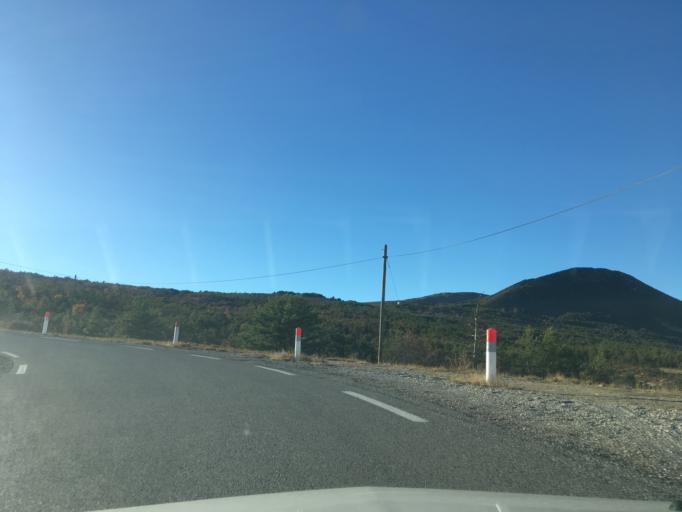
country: FR
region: Provence-Alpes-Cote d'Azur
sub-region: Departement des Alpes-de-Haute-Provence
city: Castellane
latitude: 43.7486
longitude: 6.4347
